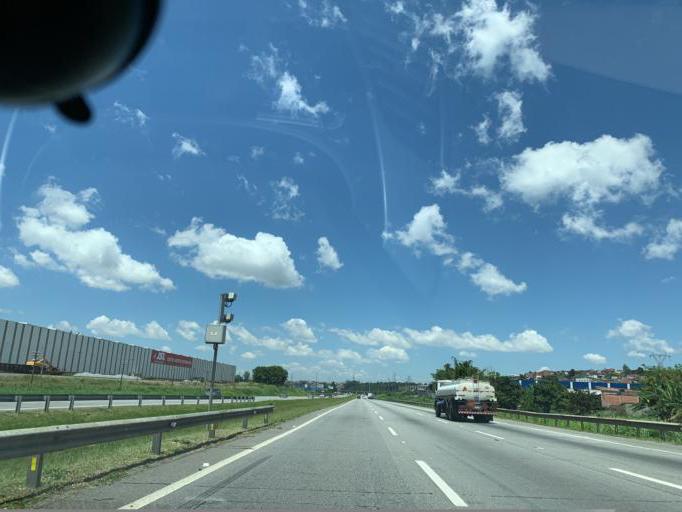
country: BR
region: Sao Paulo
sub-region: Aruja
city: Aruja
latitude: -23.4441
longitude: -46.3110
